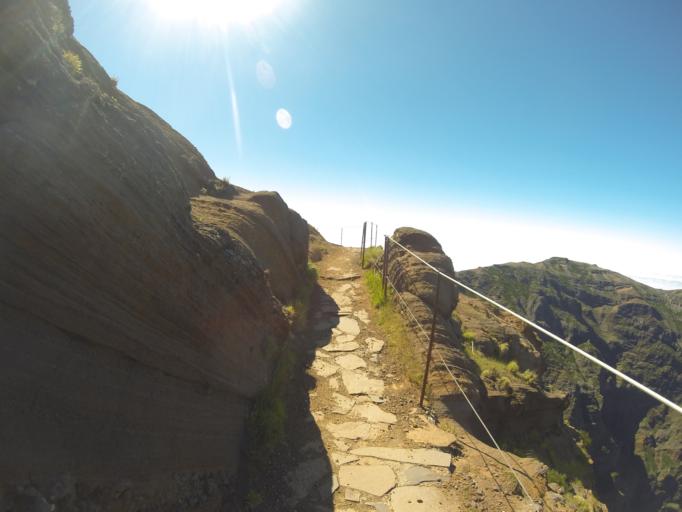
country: PT
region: Madeira
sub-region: Camara de Lobos
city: Curral das Freiras
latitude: 32.7389
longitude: -16.9359
